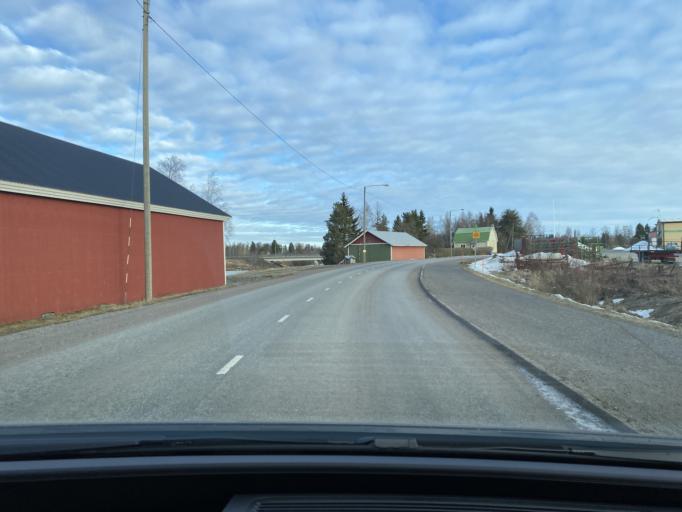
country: FI
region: Satakunta
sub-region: Pori
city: Huittinen
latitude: 61.1658
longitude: 22.6880
